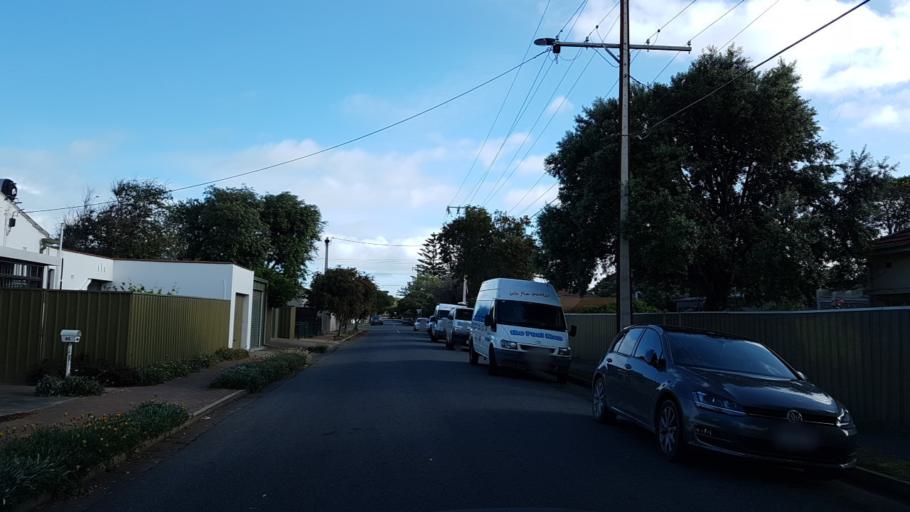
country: AU
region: South Australia
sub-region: Holdfast Bay
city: North Brighton
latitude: -34.9991
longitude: 138.5154
